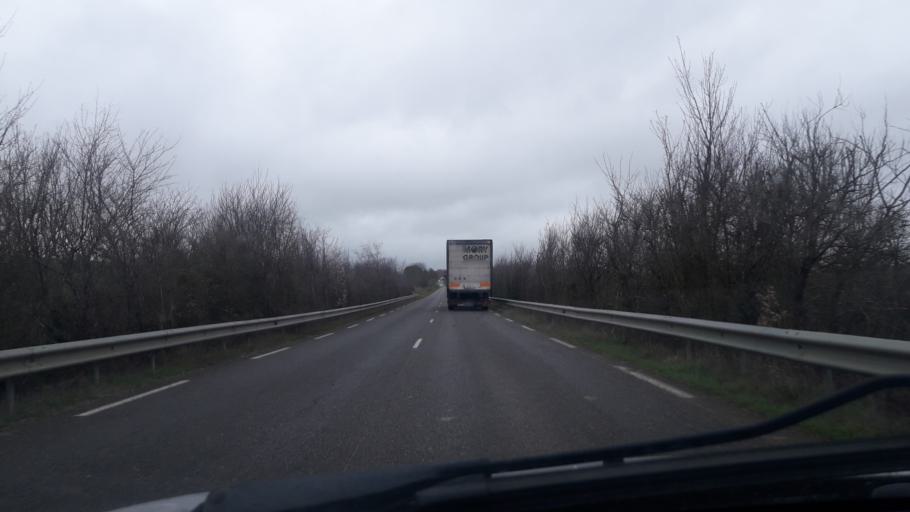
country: FR
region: Midi-Pyrenees
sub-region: Departement du Gers
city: Gimont
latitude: 43.7087
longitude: 0.9900
